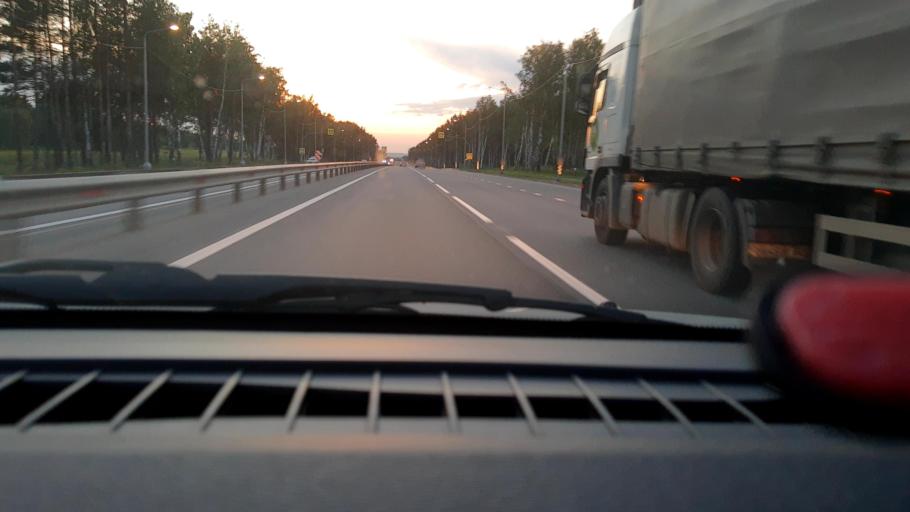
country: RU
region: Nizjnij Novgorod
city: Burevestnik
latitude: 56.0520
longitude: 43.9511
